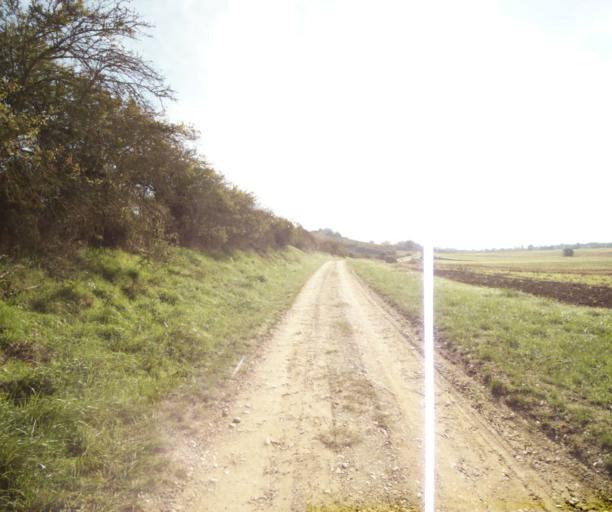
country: FR
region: Midi-Pyrenees
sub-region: Departement du Tarn-et-Garonne
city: Nohic
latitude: 43.9218
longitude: 1.4390
